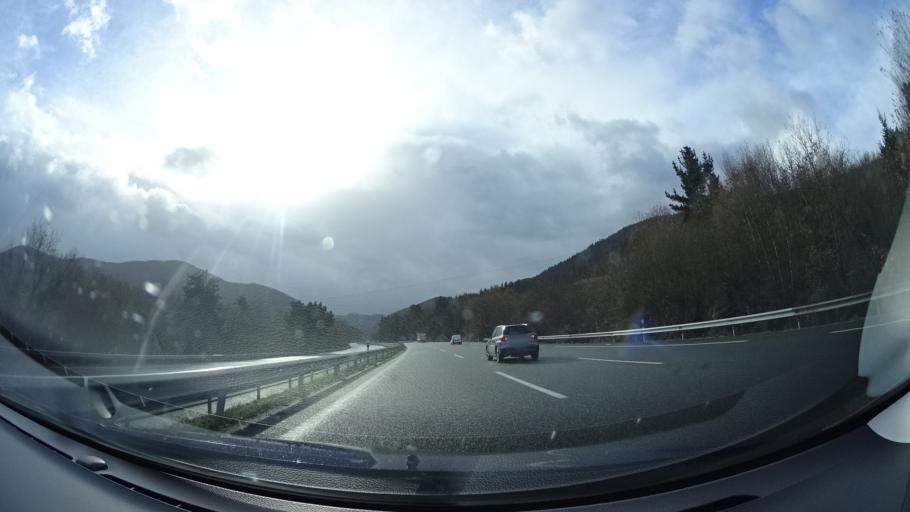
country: ES
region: Basque Country
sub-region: Bizkaia
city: Elexalde
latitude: 43.1092
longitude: -2.9148
